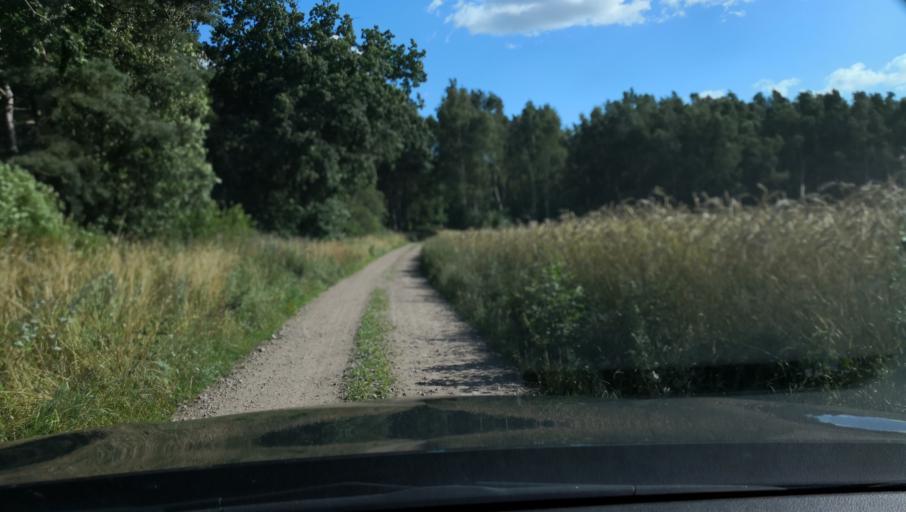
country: SE
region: Skane
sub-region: Kristianstads Kommun
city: Degeberga
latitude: 55.7997
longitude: 14.1956
